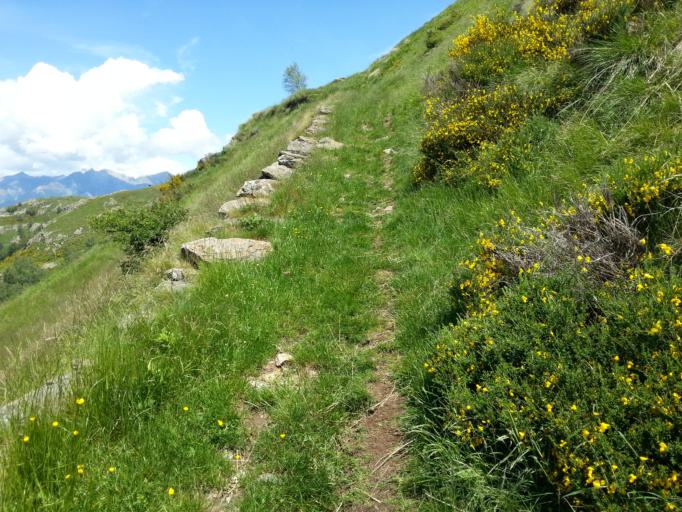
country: CH
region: Ticino
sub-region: Lugano District
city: Tesserete
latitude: 46.0968
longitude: 8.9807
